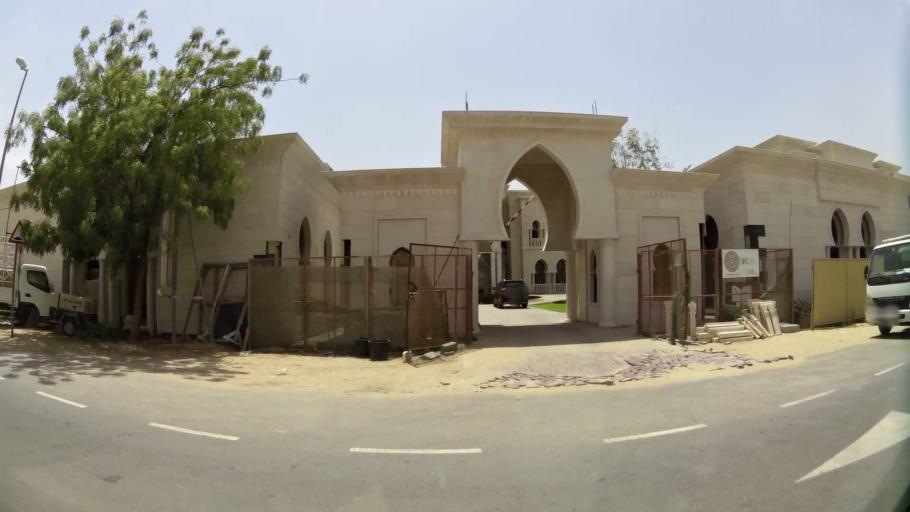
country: AE
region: Ash Shariqah
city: Sharjah
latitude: 25.2431
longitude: 55.4984
